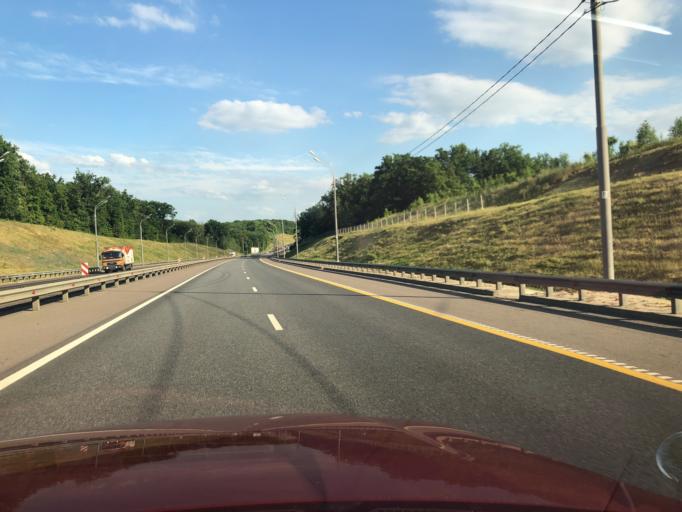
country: RU
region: Lipetsk
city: Zadonsk
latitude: 52.4089
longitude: 38.8513
